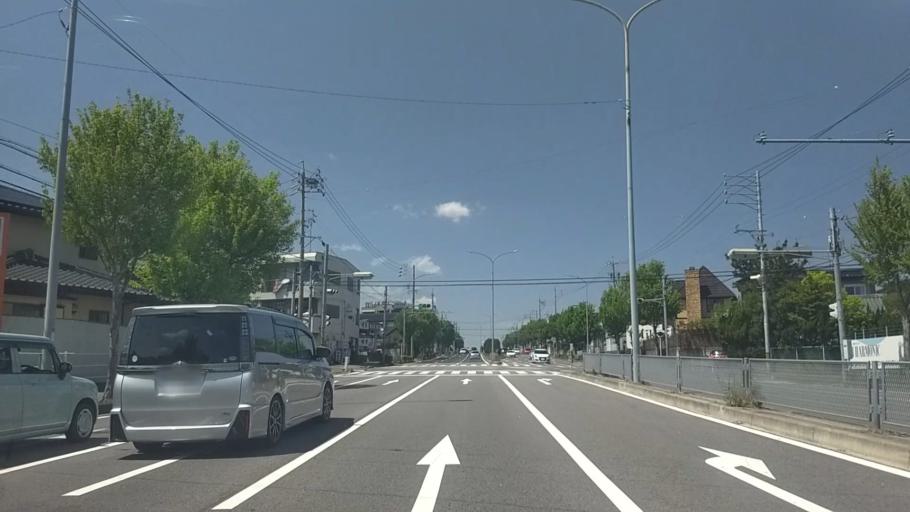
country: JP
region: Aichi
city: Okazaki
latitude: 34.9705
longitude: 137.1803
